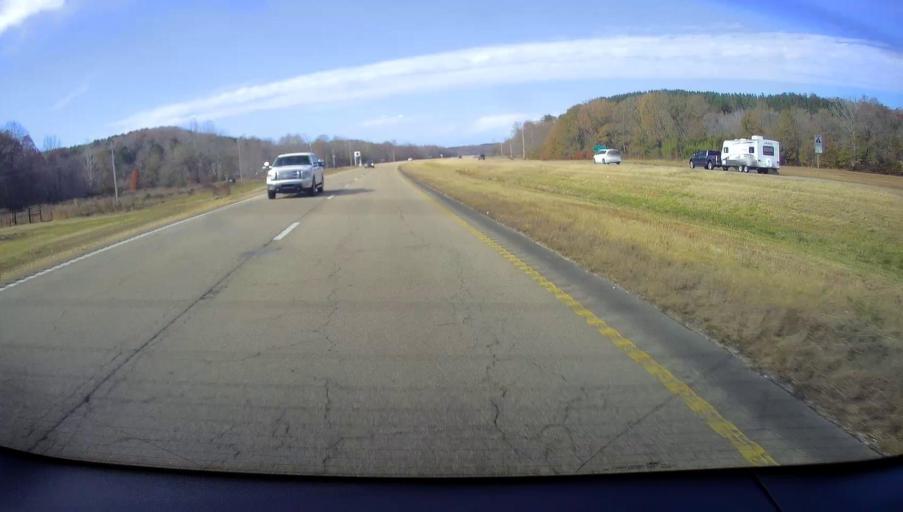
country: US
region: Mississippi
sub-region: Alcorn County
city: Corinth
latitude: 34.9341
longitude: -88.7709
